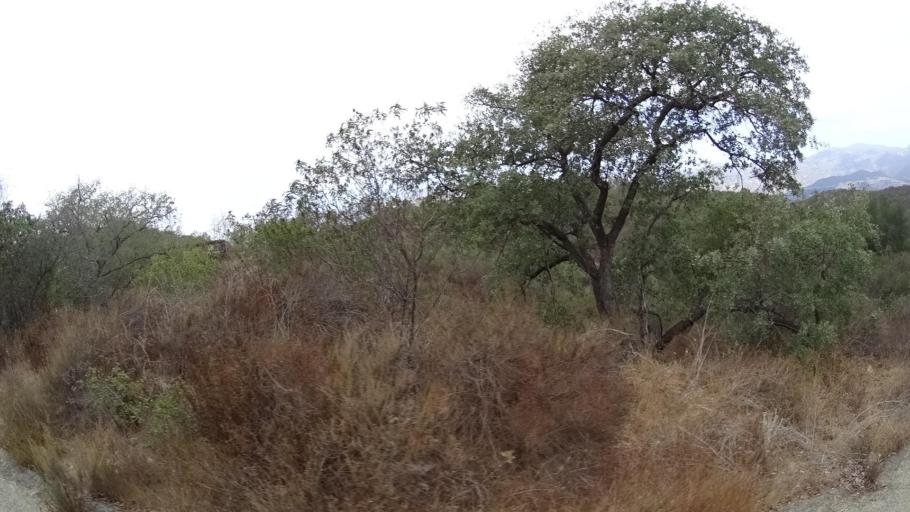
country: US
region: California
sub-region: San Diego County
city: Fallbrook
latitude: 33.4363
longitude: -117.3095
